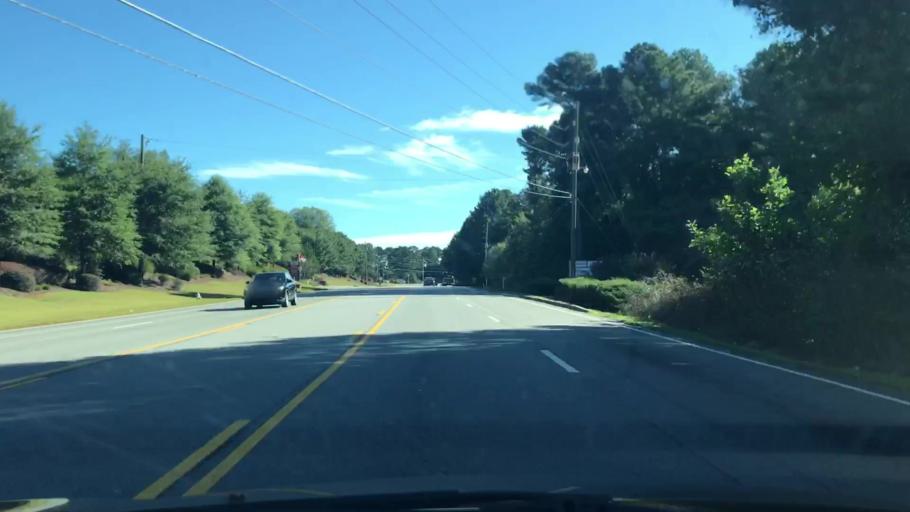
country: US
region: Georgia
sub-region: Gwinnett County
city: Mountain Park
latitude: 33.8149
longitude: -84.1101
